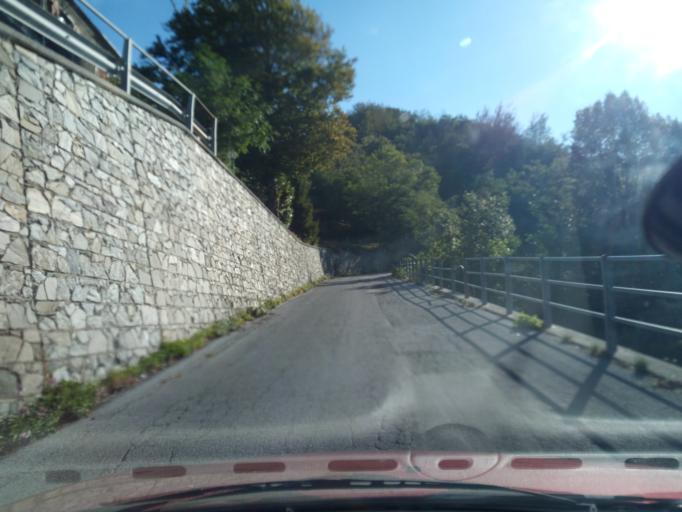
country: IT
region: Liguria
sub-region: Provincia di Genova
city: Campomorone
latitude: 44.4905
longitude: 8.8555
